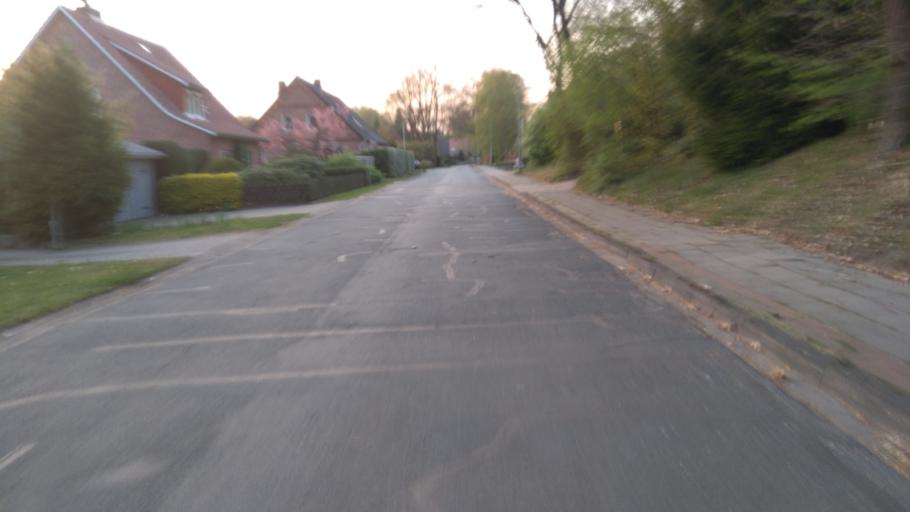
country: DE
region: Lower Saxony
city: Harsefeld
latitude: 53.4822
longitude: 9.5186
